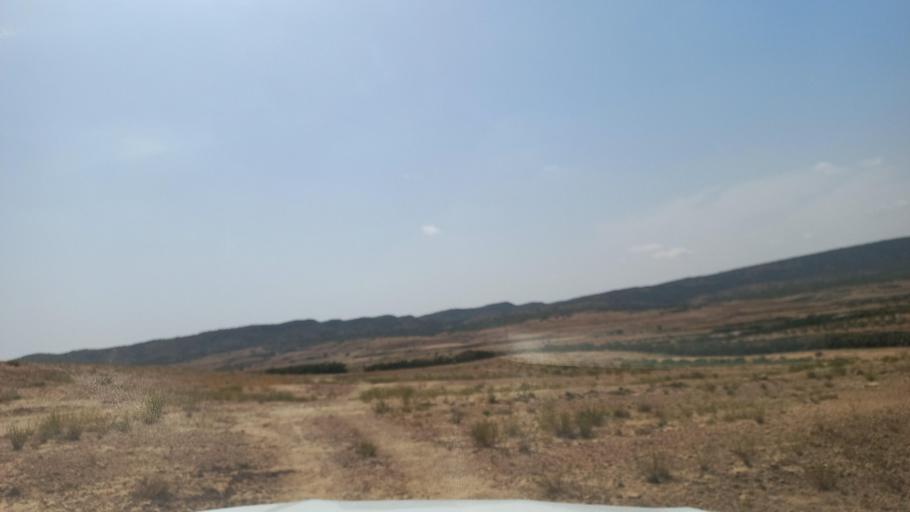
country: TN
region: Al Qasrayn
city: Sbiba
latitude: 35.3984
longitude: 8.9737
